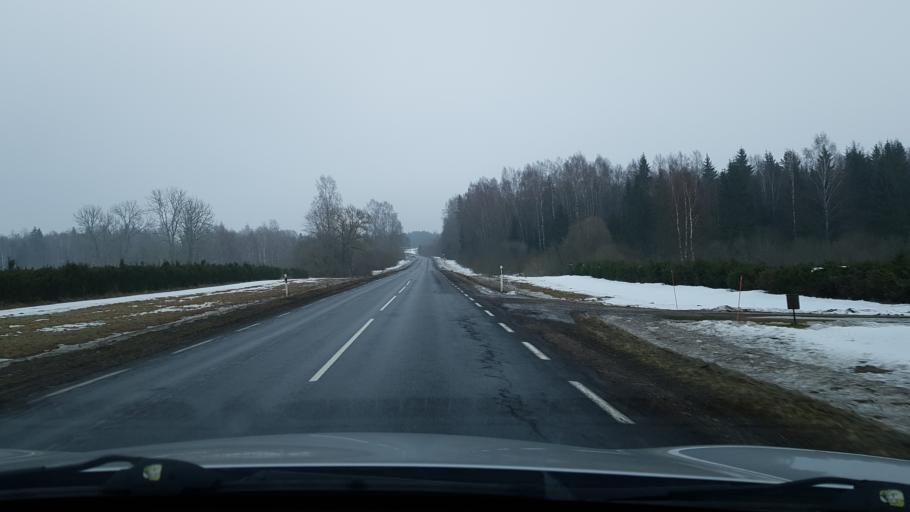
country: EE
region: Viljandimaa
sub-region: Viiratsi vald
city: Viiratsi
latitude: 58.2527
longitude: 25.7344
